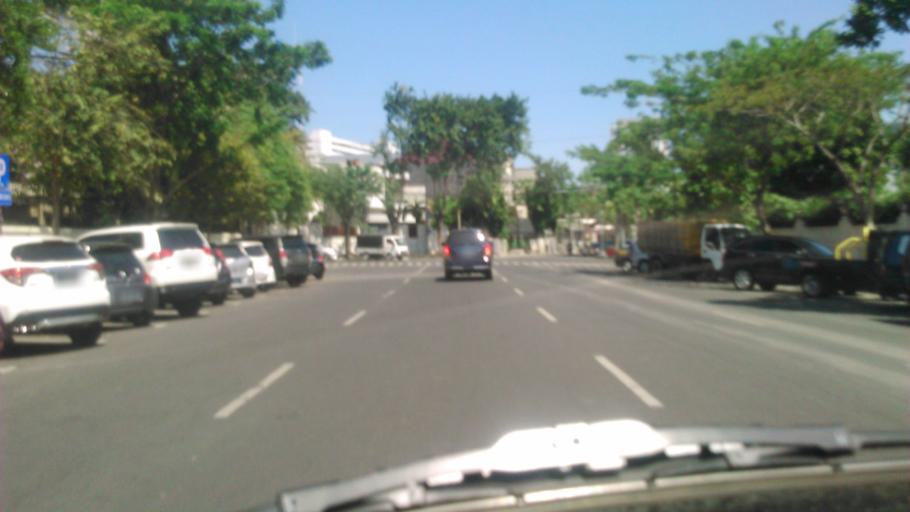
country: ID
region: East Java
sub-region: Kota Surabaya
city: Surabaya
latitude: -7.2576
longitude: 112.7491
